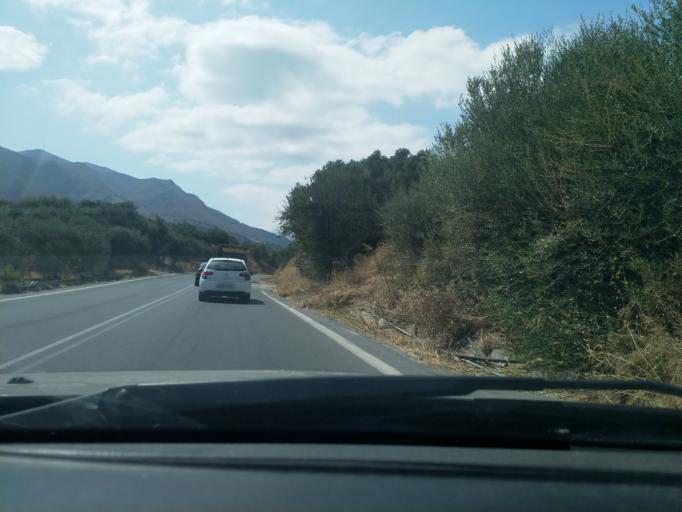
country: GR
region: Crete
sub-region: Nomos Rethymnis
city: Atsipopoulon
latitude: 35.2242
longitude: 24.4840
